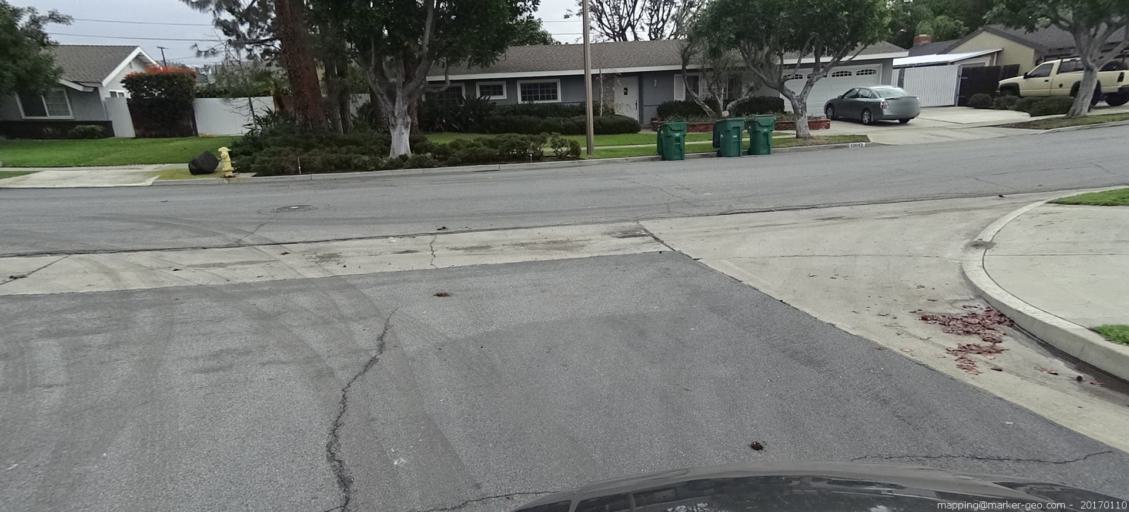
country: US
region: California
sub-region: Orange County
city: Tustin
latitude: 33.7727
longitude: -117.8293
